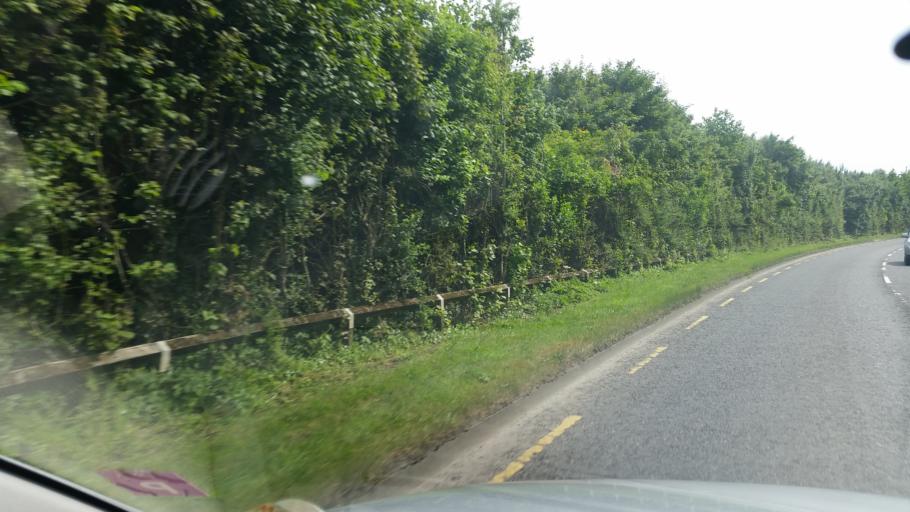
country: IE
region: Leinster
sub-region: Dublin City
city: Finglas
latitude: 53.4311
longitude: -6.2983
